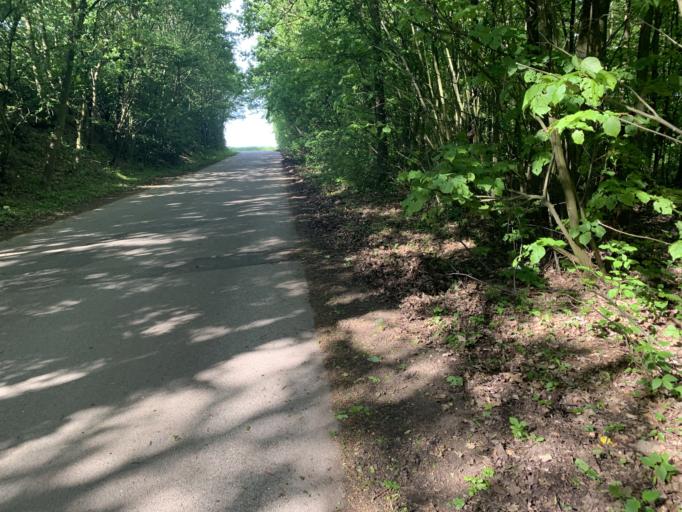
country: DE
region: North Rhine-Westphalia
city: Tuernich
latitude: 50.8760
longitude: 6.7916
